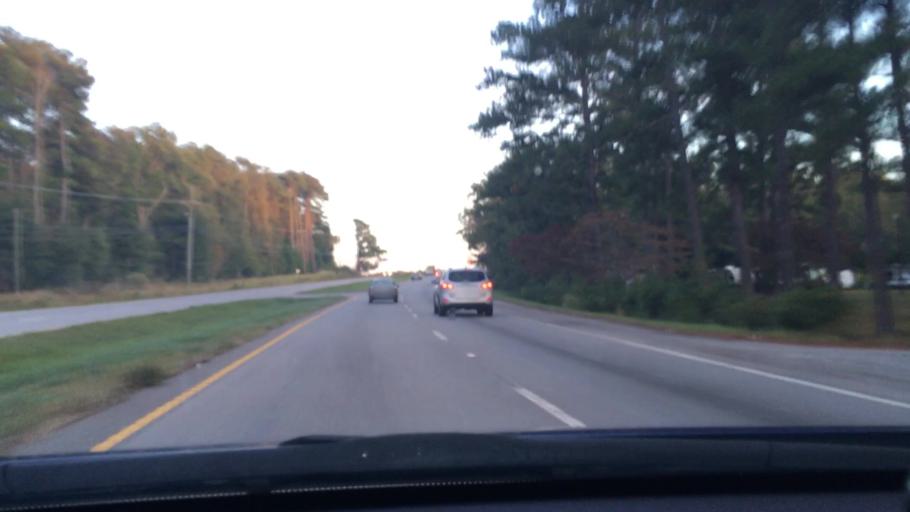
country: US
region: South Carolina
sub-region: Richland County
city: Hopkins
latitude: 33.9517
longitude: -80.8246
